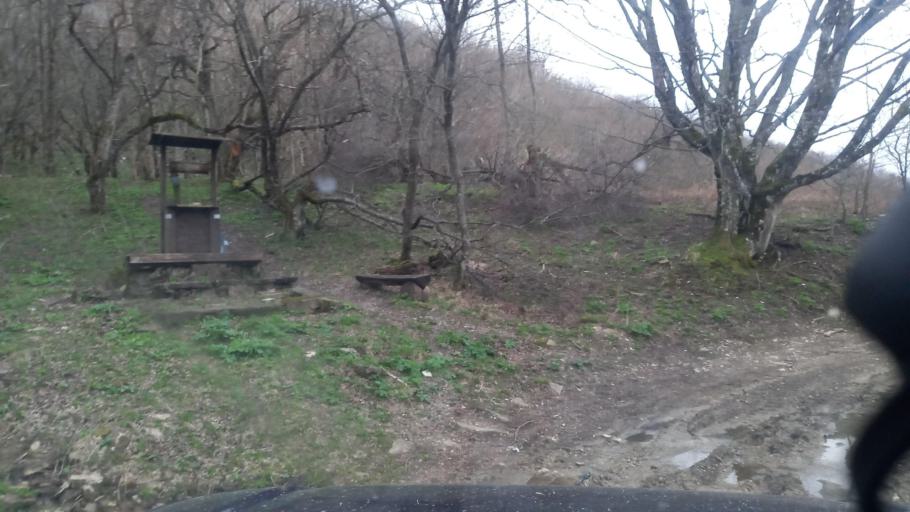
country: RU
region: Krasnodarskiy
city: Pshada
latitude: 44.5980
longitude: 38.2815
